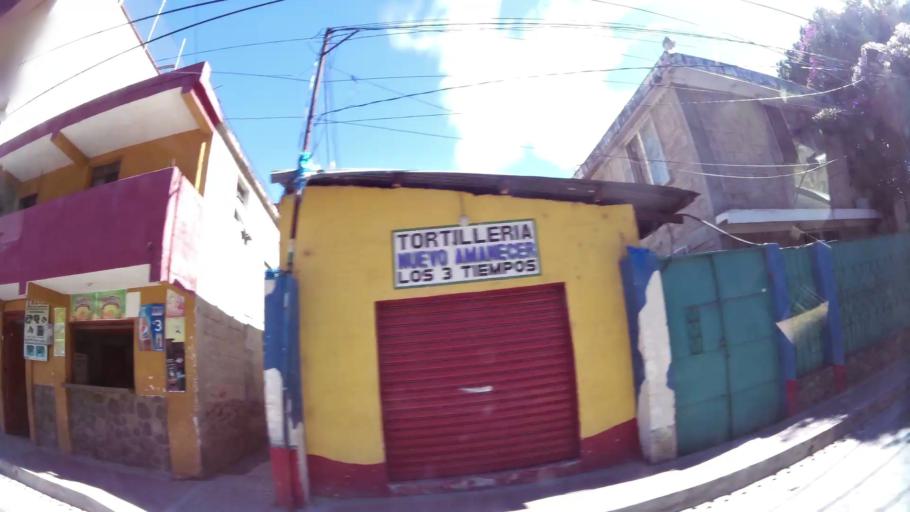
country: GT
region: Solola
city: Panajachel
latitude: 14.7379
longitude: -91.1587
